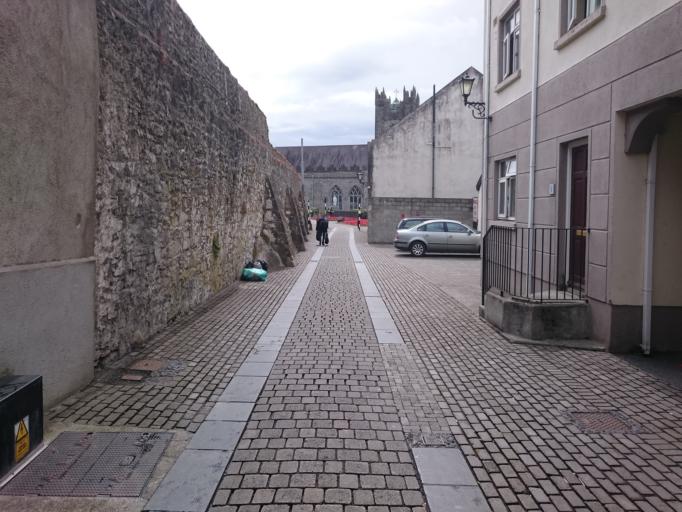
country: IE
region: Leinster
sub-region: Kilkenny
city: Kilkenny
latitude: 52.6545
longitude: -7.2564
